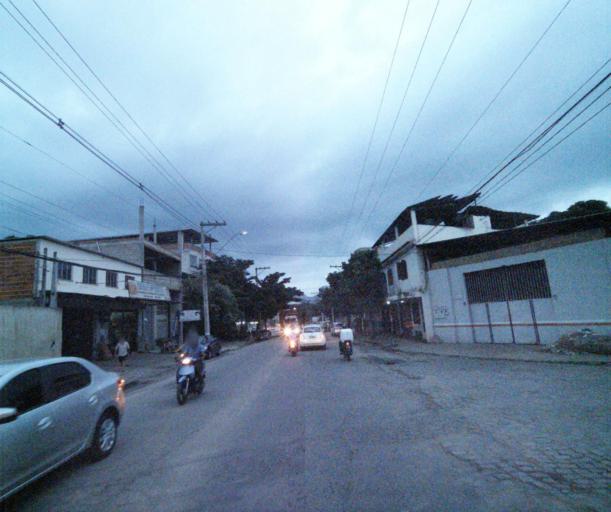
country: BR
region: Espirito Santo
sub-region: Castelo
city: Castelo
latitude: -20.6175
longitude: -41.2043
